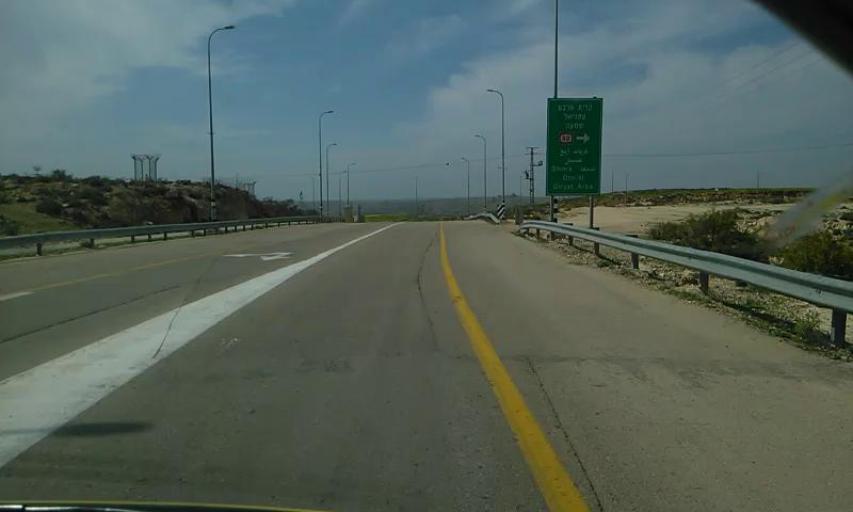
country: PS
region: West Bank
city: Az Zahiriyah
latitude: 31.3767
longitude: 35.0050
